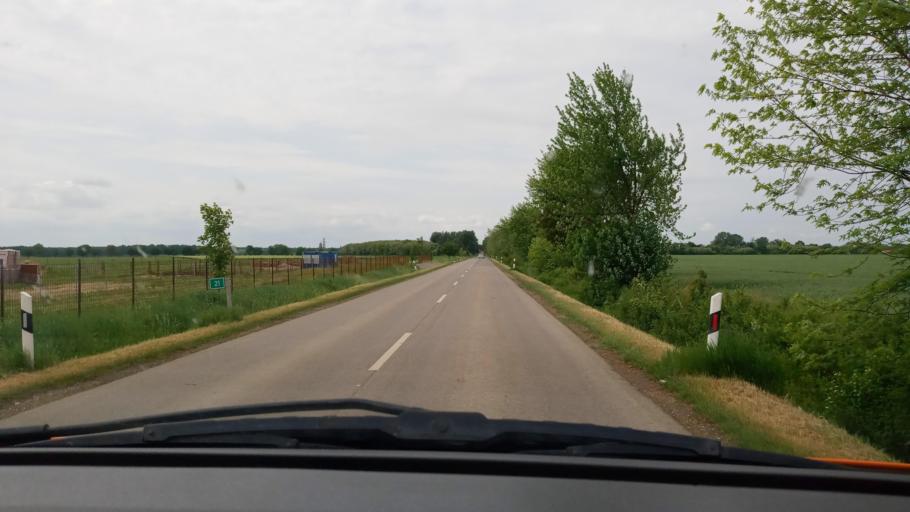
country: HU
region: Baranya
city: Vajszlo
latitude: 45.9131
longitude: 18.0516
